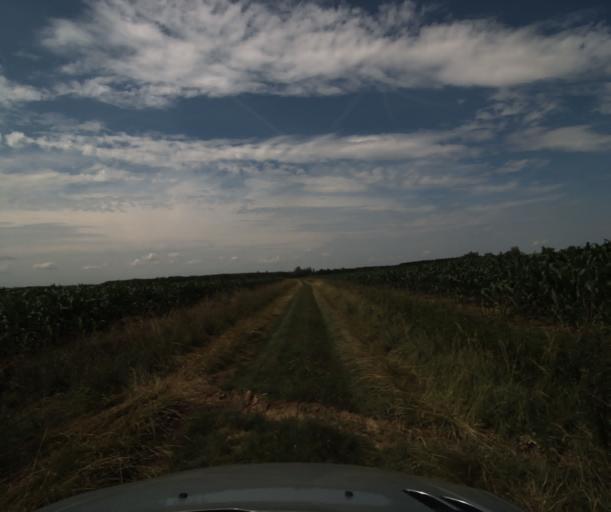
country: FR
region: Midi-Pyrenees
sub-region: Departement de la Haute-Garonne
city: Labastidette
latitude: 43.4814
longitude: 1.2223
